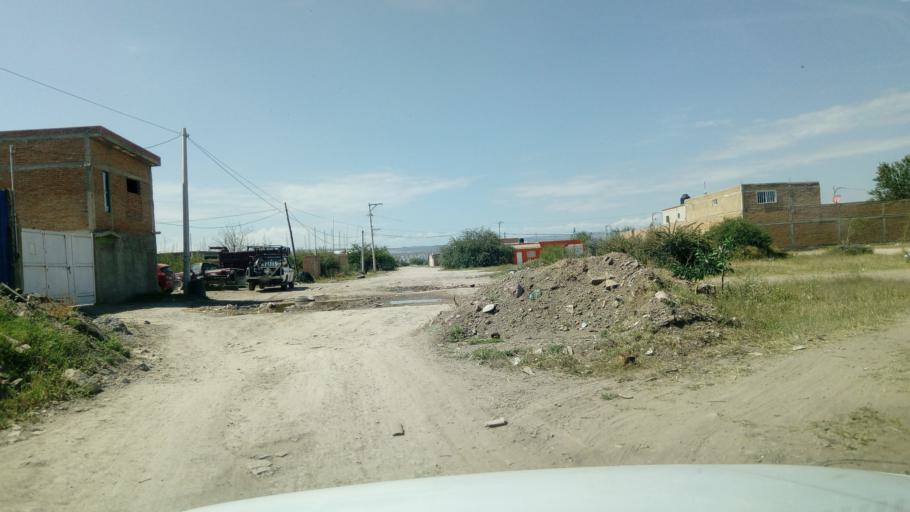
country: MX
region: Durango
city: Victoria de Durango
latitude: 23.9893
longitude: -104.6828
